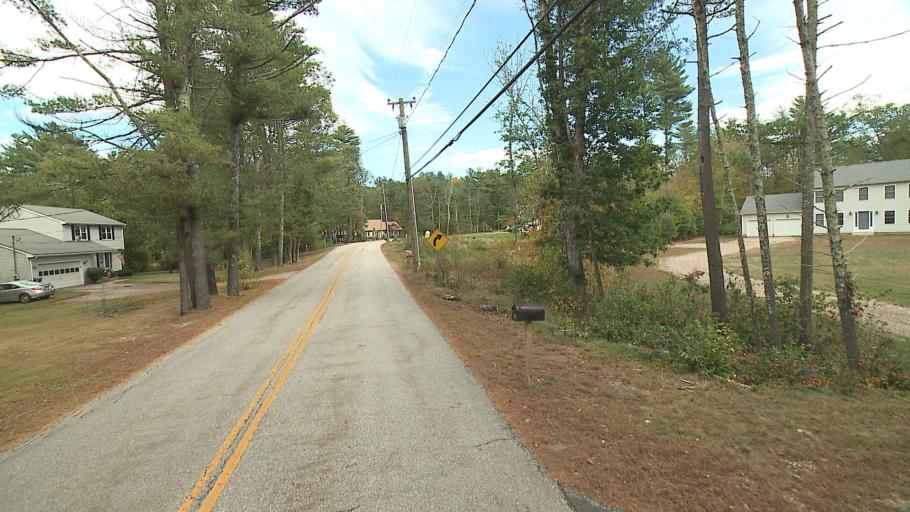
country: US
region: Connecticut
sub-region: Windham County
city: Thompson
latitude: 41.9487
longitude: -71.8180
